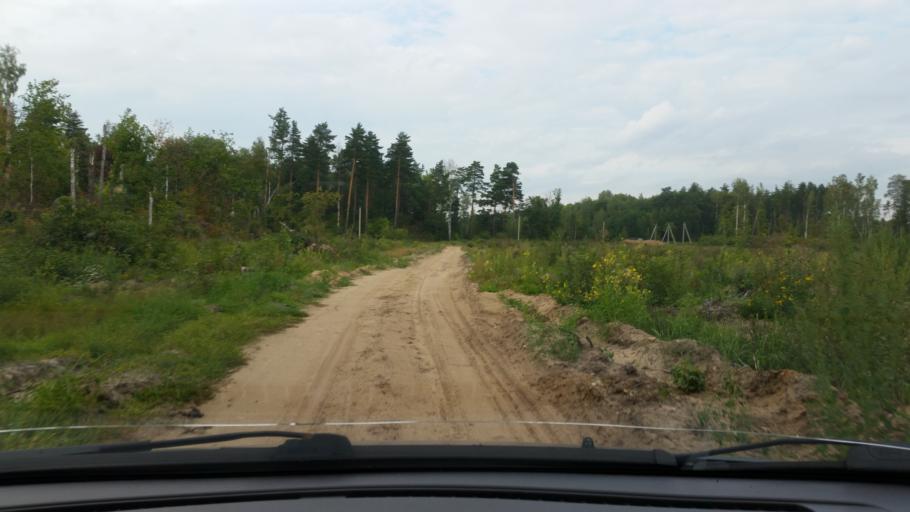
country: RU
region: Moskovskaya
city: Bol'shoye Gryzlovo
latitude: 54.8527
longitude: 37.7135
